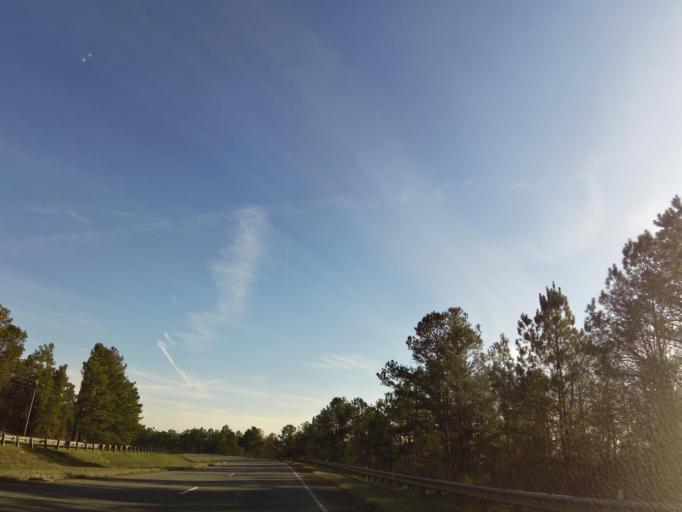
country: US
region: Georgia
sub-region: Stewart County
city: Richland
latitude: 32.1550
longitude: -84.6967
